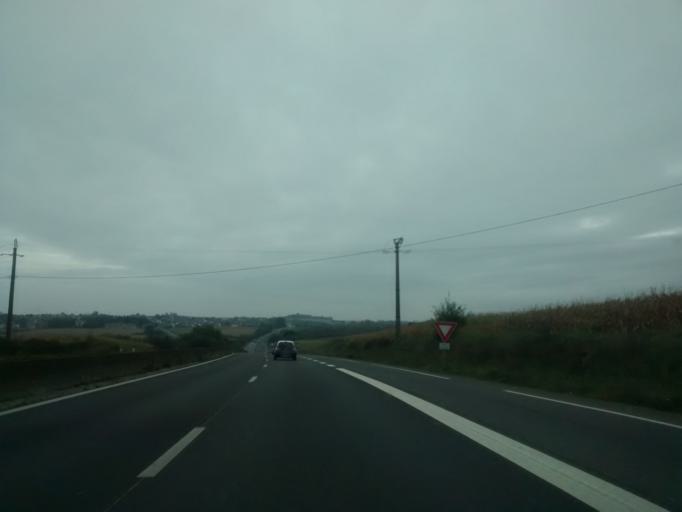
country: FR
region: Brittany
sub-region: Departement d'Ille-et-Vilaine
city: Saint-Jouan-des-Guerets
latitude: 48.5874
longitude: -1.9541
